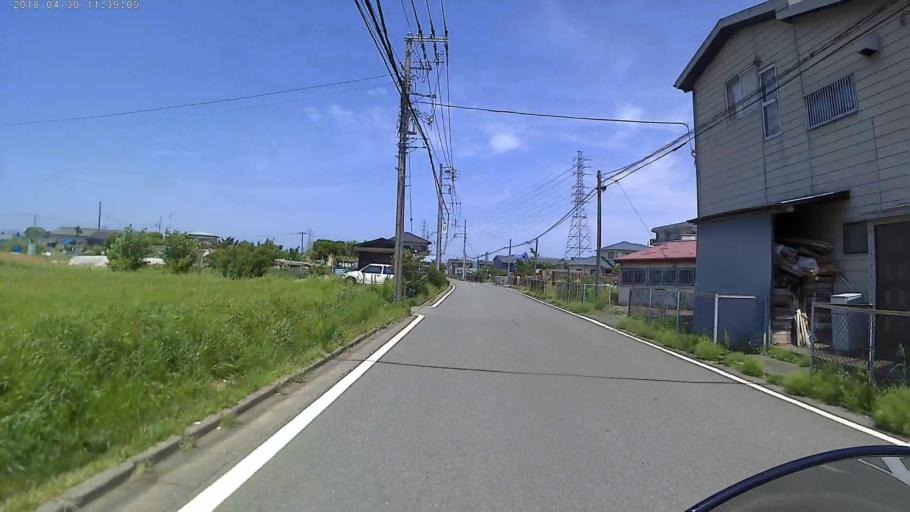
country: JP
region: Kanagawa
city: Zama
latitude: 35.4792
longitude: 139.3894
